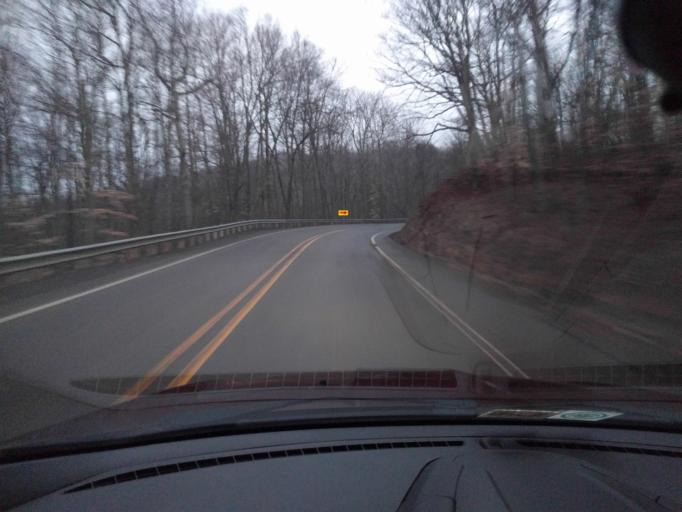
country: US
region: West Virginia
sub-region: Greenbrier County
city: Rainelle
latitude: 37.9822
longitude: -80.8399
